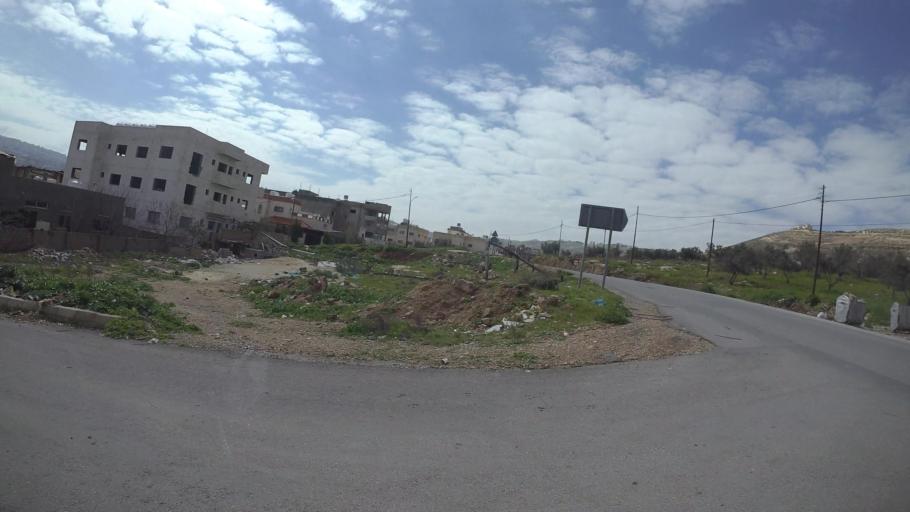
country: JO
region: Amman
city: Al Jubayhah
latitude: 32.0709
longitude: 35.8176
